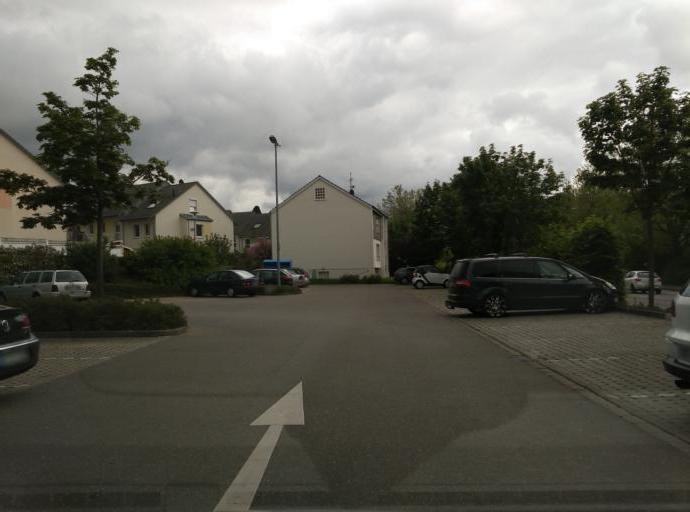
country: DE
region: Baden-Wuerttemberg
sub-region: Regierungsbezirk Stuttgart
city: Nurtingen
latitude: 48.6297
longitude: 9.3461
